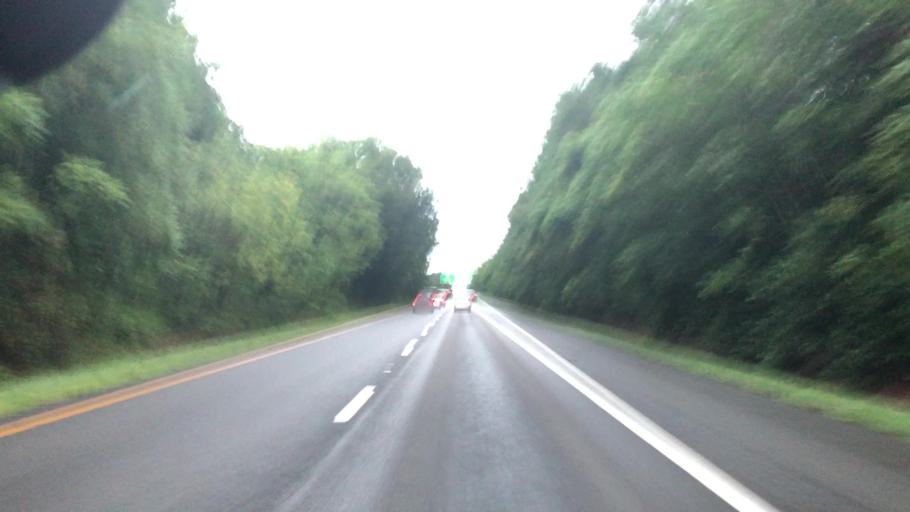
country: US
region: Virginia
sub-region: James City County
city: Williamsburg
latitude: 37.3941
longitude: -76.7730
